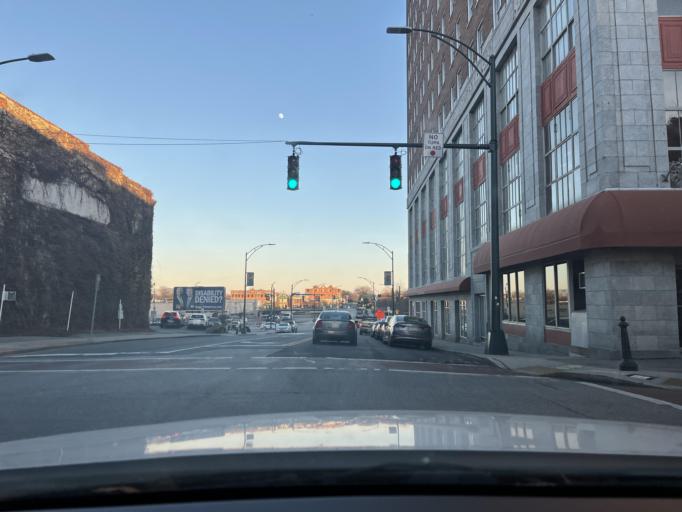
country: US
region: North Carolina
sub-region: Guilford County
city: Greensboro
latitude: 36.0702
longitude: -79.7905
